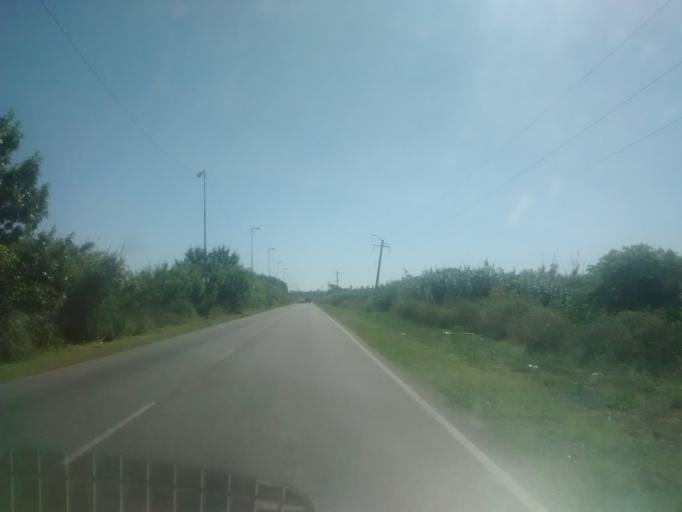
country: AR
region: Buenos Aires
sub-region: Partido de Berisso
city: Berisso
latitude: -34.9052
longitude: -57.9037
